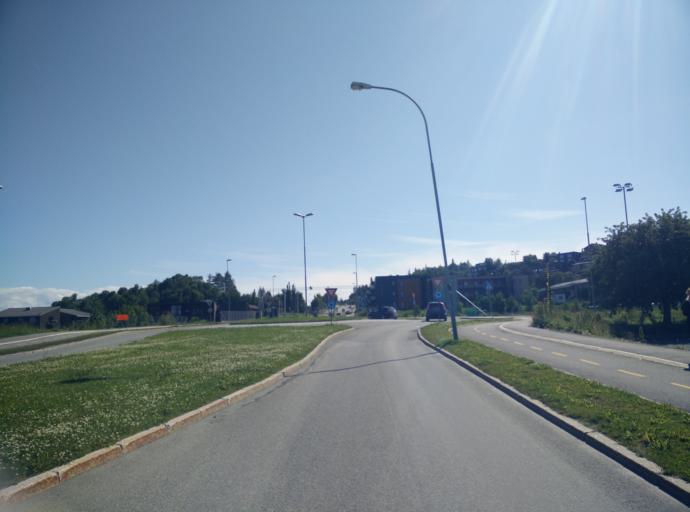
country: NO
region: Sor-Trondelag
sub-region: Trondheim
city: Trondheim
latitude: 63.4064
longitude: 10.3590
